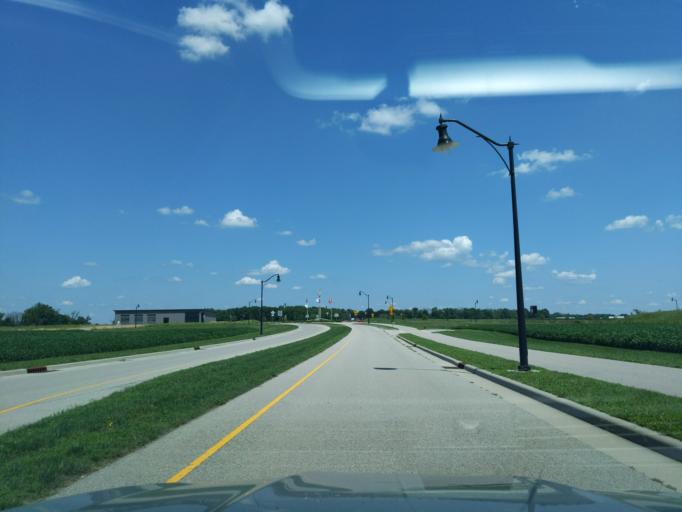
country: US
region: Indiana
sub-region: Decatur County
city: Greensburg
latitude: 39.3564
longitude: -85.5046
